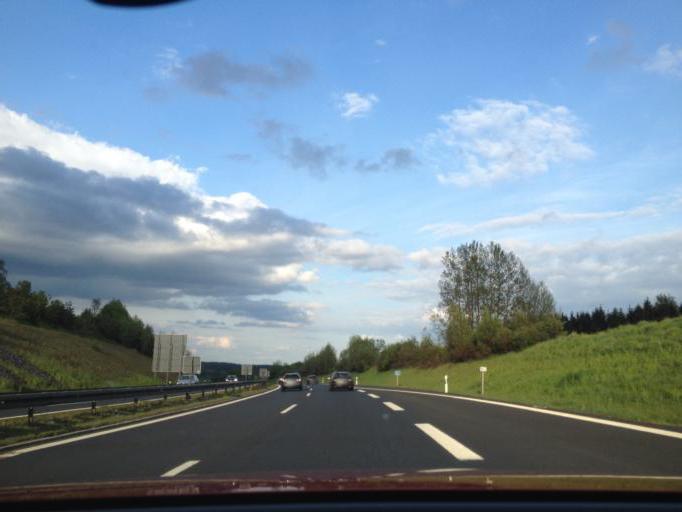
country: DE
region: Bavaria
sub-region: Upper Palatinate
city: Pechbrunn
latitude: 49.9778
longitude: 12.1401
